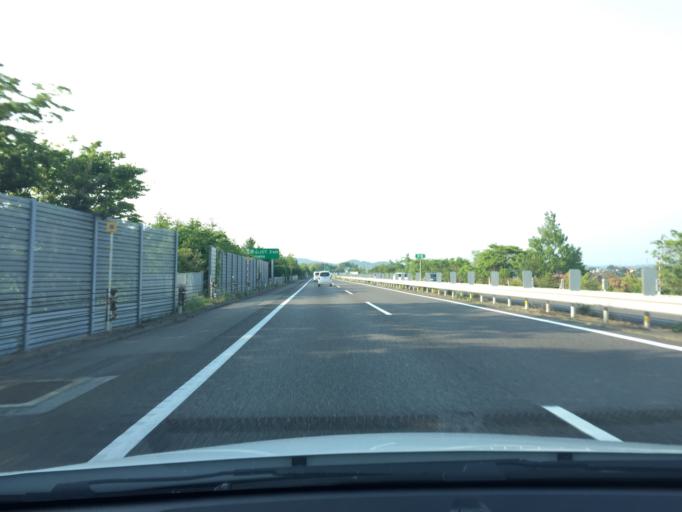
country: JP
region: Fukushima
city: Koriyama
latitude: 37.4472
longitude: 140.3524
